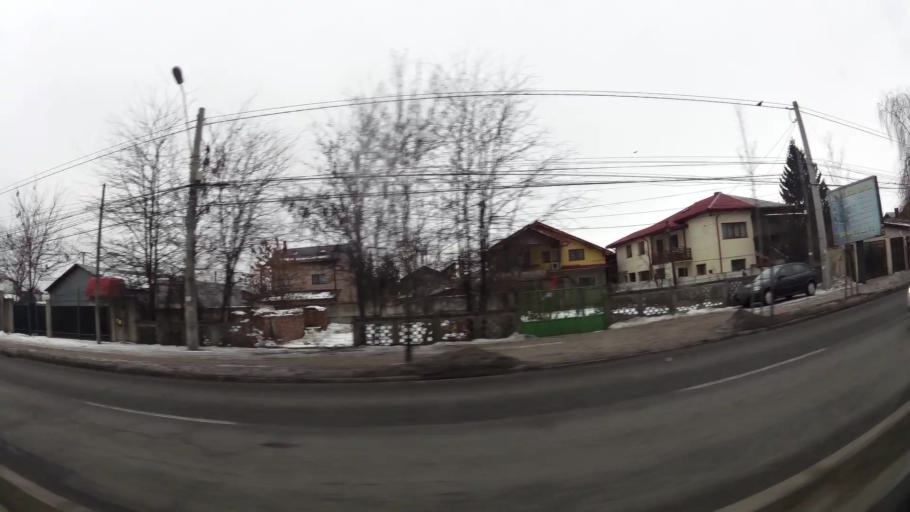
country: RO
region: Ilfov
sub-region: Comuna Chitila
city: Chitila
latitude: 44.5022
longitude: 25.9912
